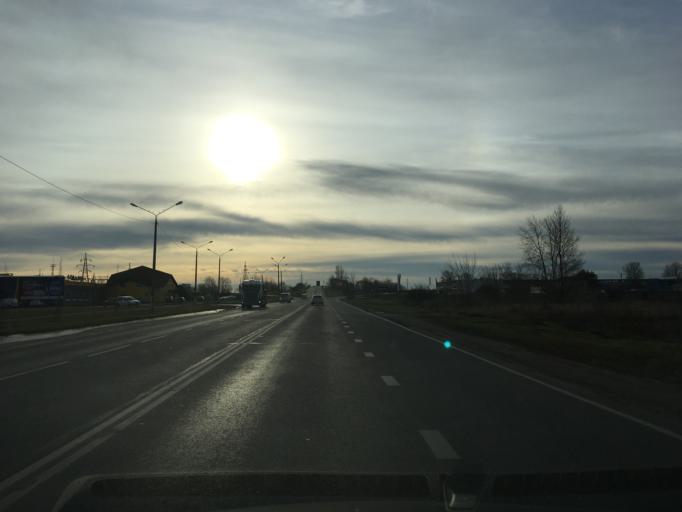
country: EE
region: Ida-Virumaa
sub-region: Narva linn
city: Narva
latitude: 59.3762
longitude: 28.1542
